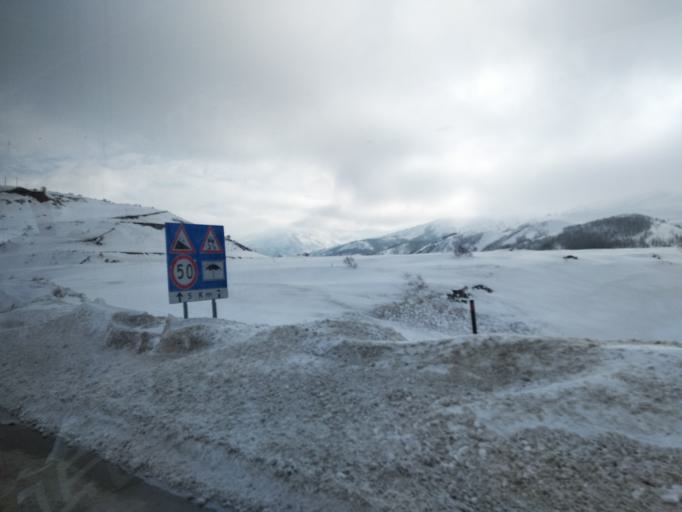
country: TR
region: Erzincan
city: Catalarmut
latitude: 39.8939
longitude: 39.3713
